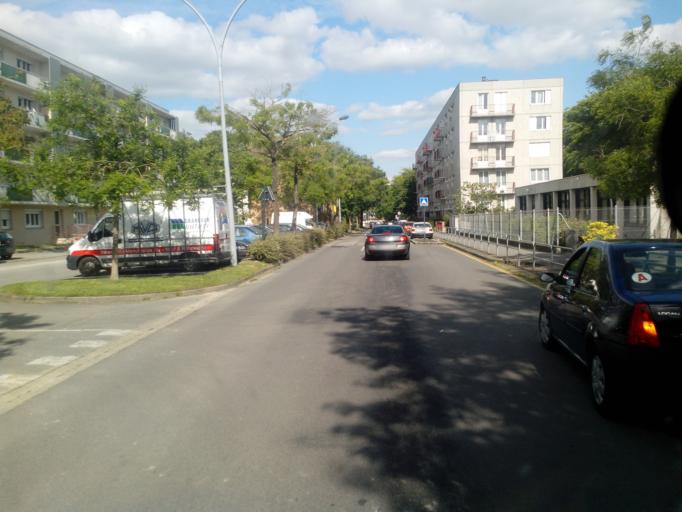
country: FR
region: Brittany
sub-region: Departement d'Ille-et-Vilaine
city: Montgermont
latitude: 48.1231
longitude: -1.7118
